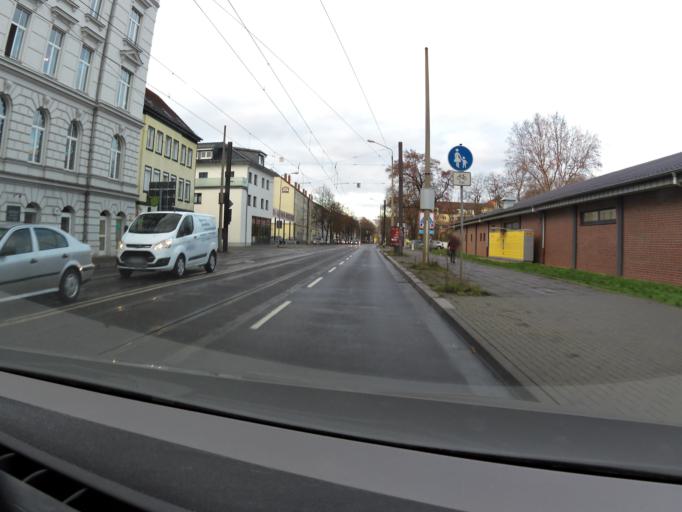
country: DE
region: Saxony-Anhalt
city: Magdeburg
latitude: 52.1297
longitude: 11.6049
